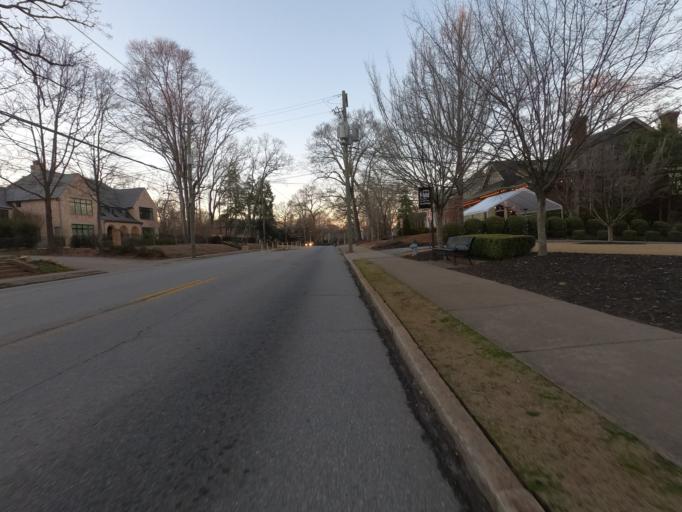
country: US
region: Georgia
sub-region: Clarke County
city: Athens
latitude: 33.9412
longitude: -83.3875
